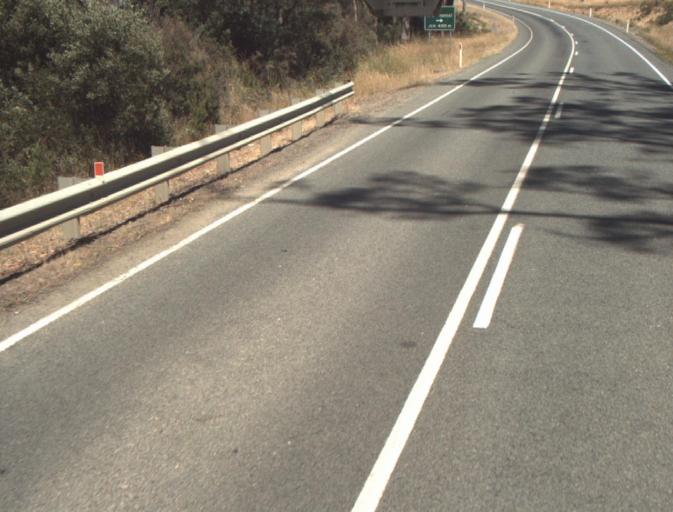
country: AU
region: Tasmania
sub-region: Launceston
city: Newstead
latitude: -41.3315
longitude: 147.3511
